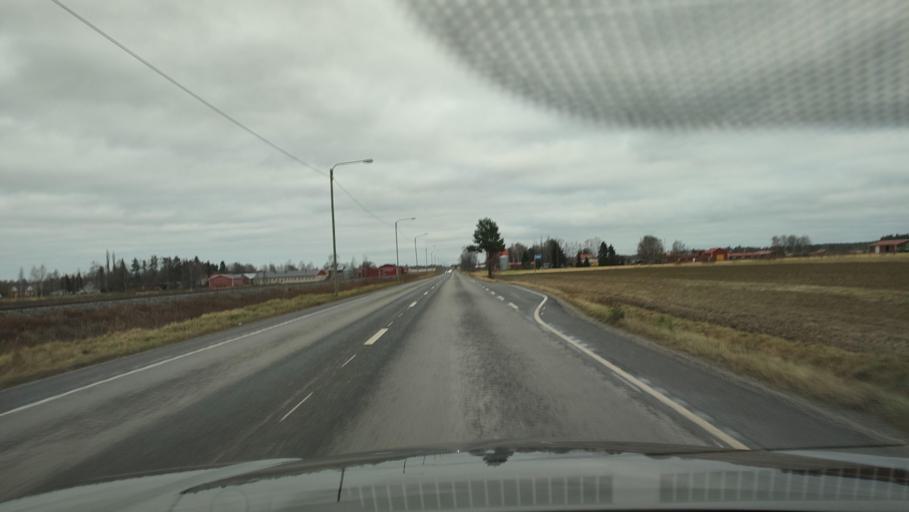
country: FI
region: Southern Ostrobothnia
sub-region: Seinaejoki
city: Ilmajoki
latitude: 62.7146
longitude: 22.5491
